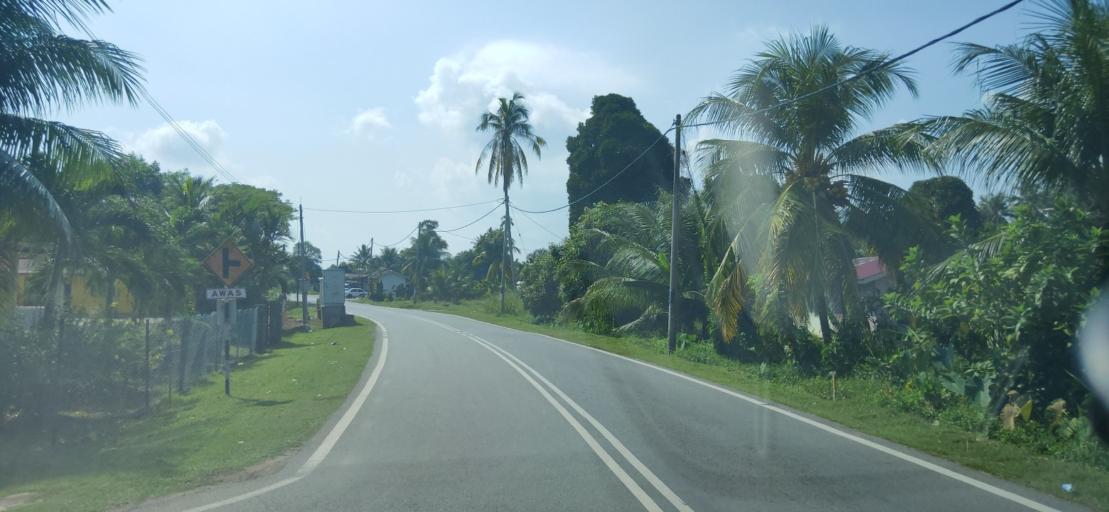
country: MY
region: Kedah
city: Sungai Petani
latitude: 5.6587
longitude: 100.4765
